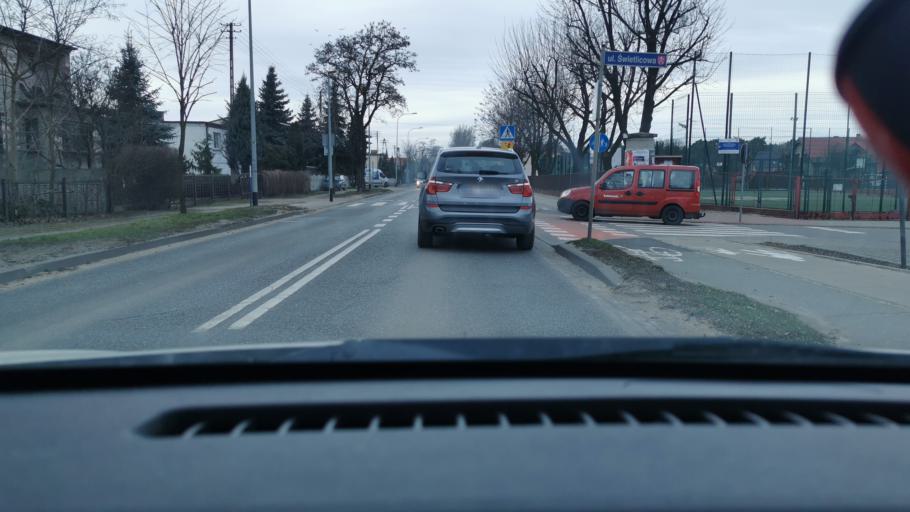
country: PL
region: Greater Poland Voivodeship
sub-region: Powiat ostrowski
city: Ostrow Wielkopolski
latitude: 51.6437
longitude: 17.8632
